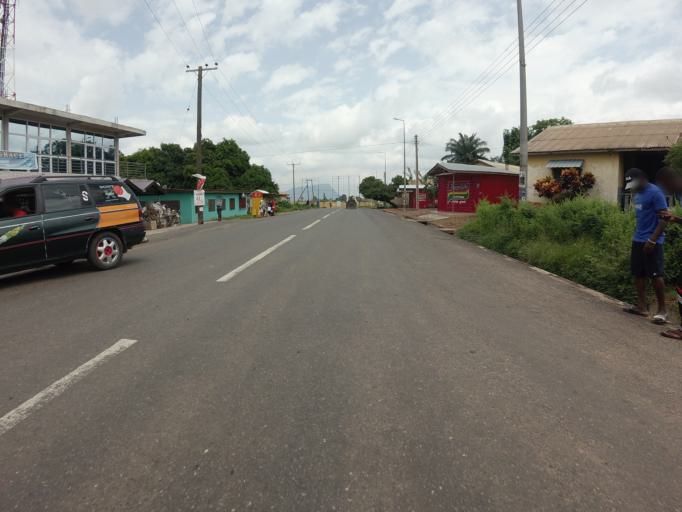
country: GH
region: Volta
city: Ho
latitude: 6.6042
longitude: 0.4660
